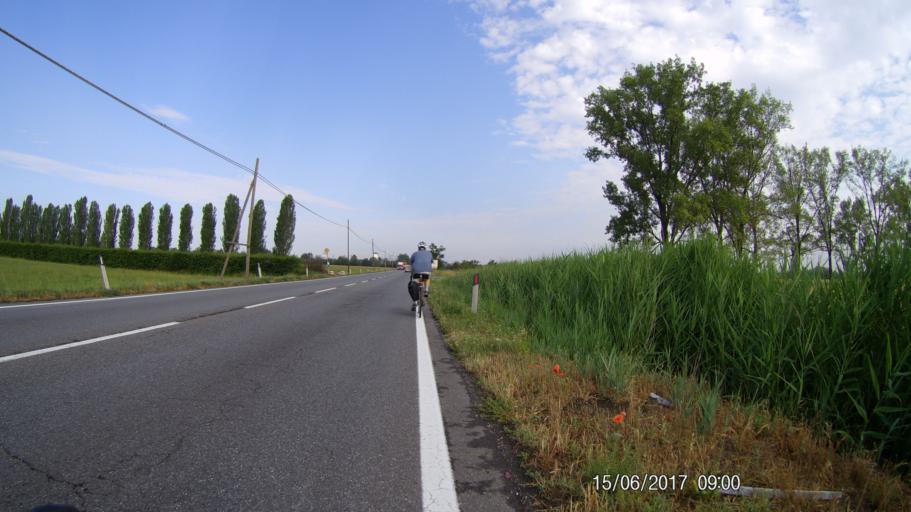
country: IT
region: Emilia-Romagna
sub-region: Provincia di Reggio Emilia
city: Calerno
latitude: 44.7546
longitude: 10.4699
